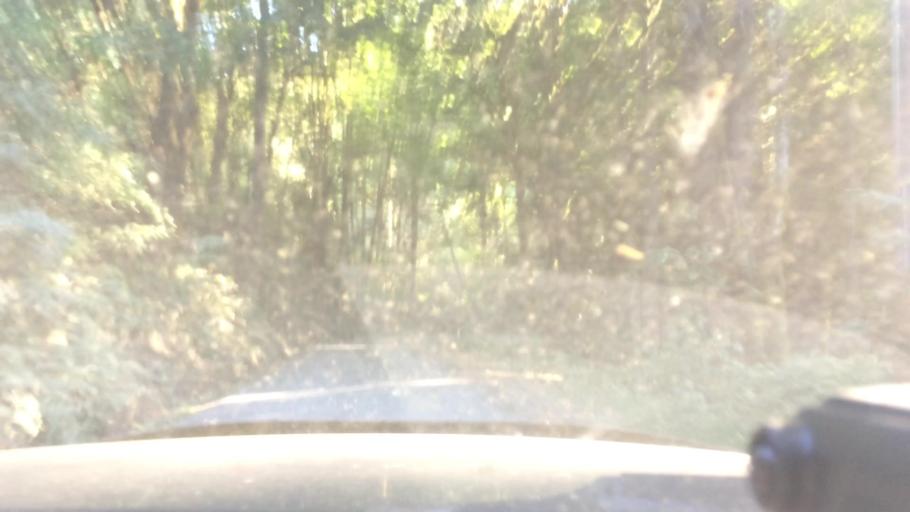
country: US
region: Oregon
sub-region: Yamhill County
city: Newberg
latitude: 45.3614
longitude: -122.9761
